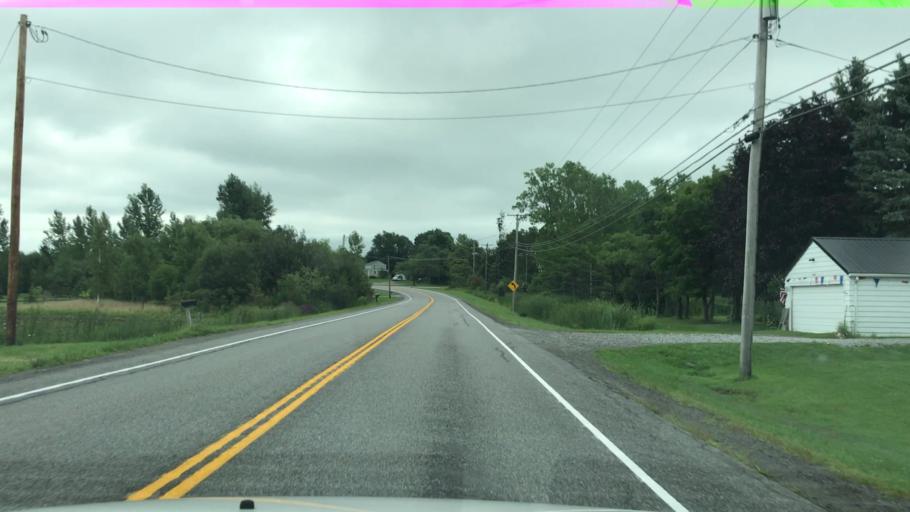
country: US
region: New York
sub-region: Wyoming County
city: Attica
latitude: 42.8363
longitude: -78.3396
